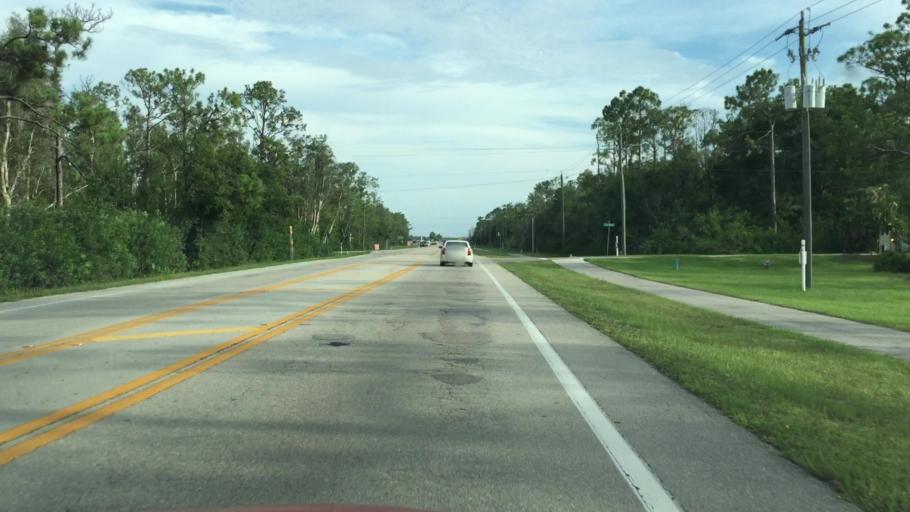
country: US
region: Florida
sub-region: Lee County
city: Fort Myers
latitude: 26.6206
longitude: -81.8116
